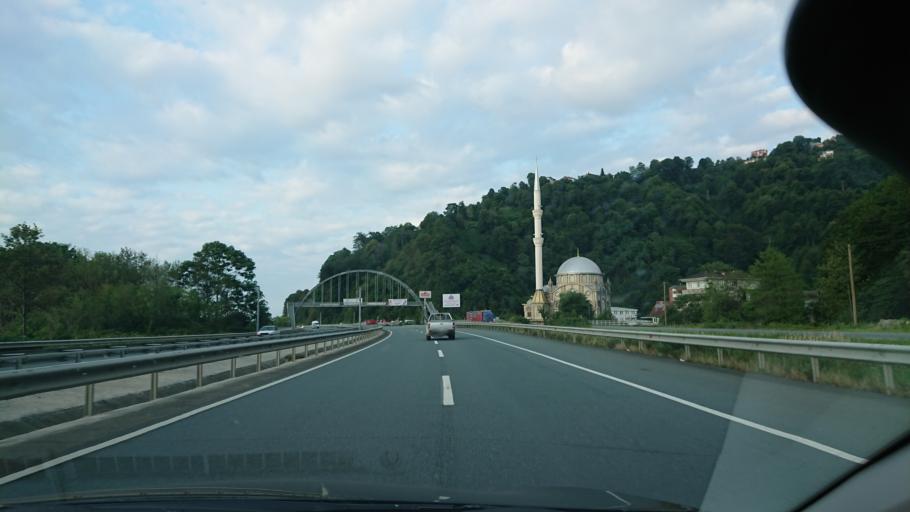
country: TR
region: Rize
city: Cayeli
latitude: 41.1552
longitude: 40.7941
